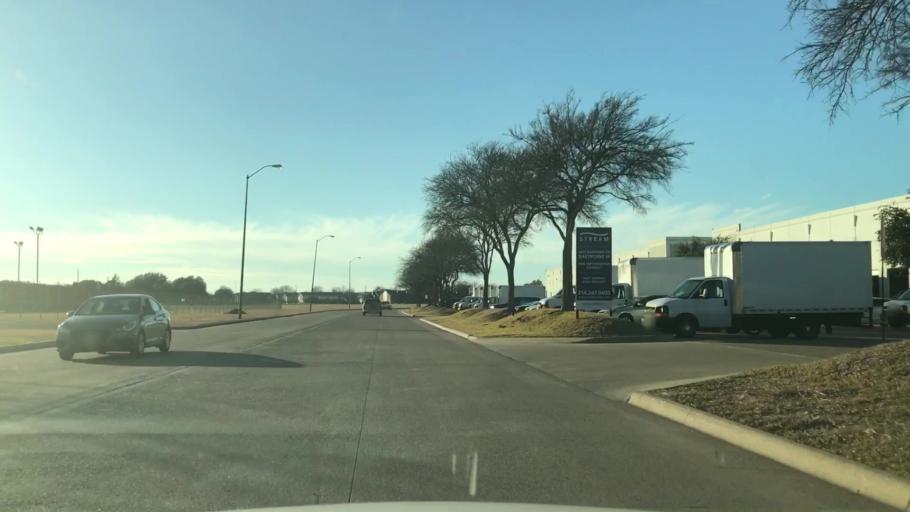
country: US
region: Texas
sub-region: Dallas County
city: Balch Springs
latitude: 32.7843
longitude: -96.6787
